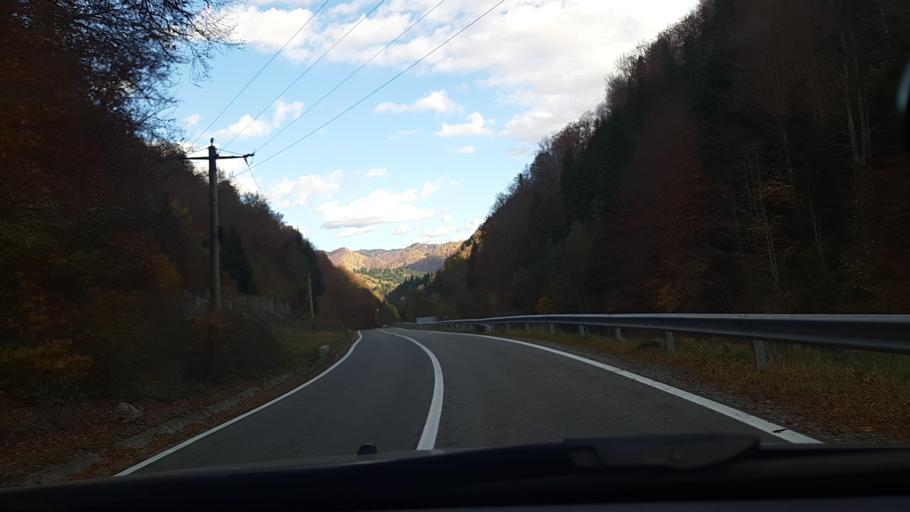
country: RO
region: Valcea
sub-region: Comuna Voineasa
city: Voineasa
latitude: 45.4236
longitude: 23.9276
